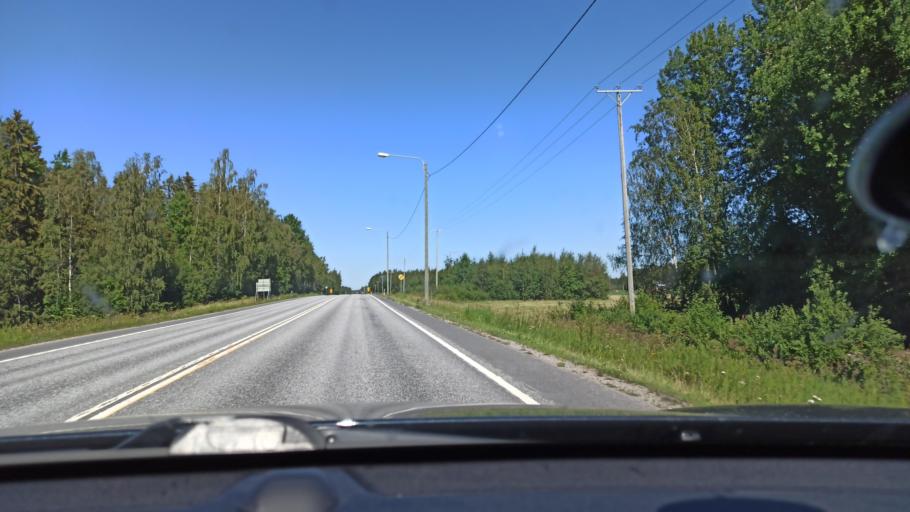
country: FI
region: Ostrobothnia
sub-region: Vaasa
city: Voera
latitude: 63.2293
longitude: 22.2409
